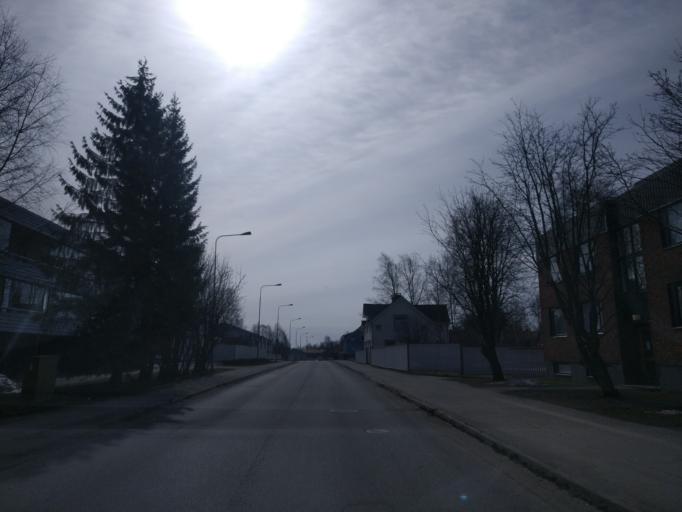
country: FI
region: Lapland
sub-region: Kemi-Tornio
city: Kemi
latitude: 65.7453
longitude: 24.5645
